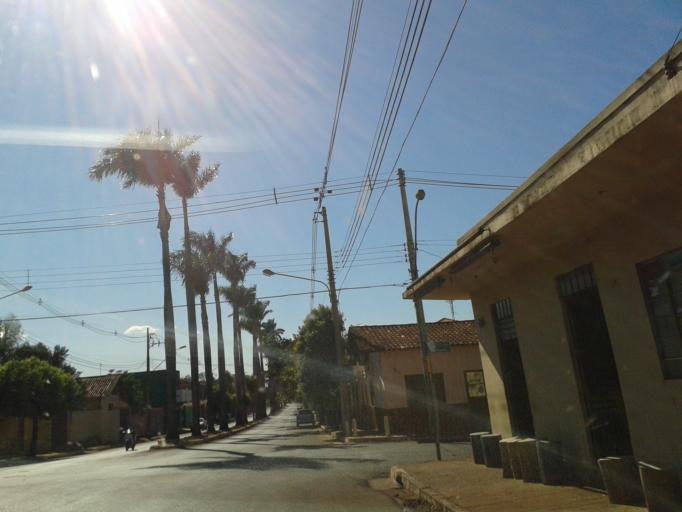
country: BR
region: Minas Gerais
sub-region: Centralina
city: Centralina
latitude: -18.5831
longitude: -49.1983
